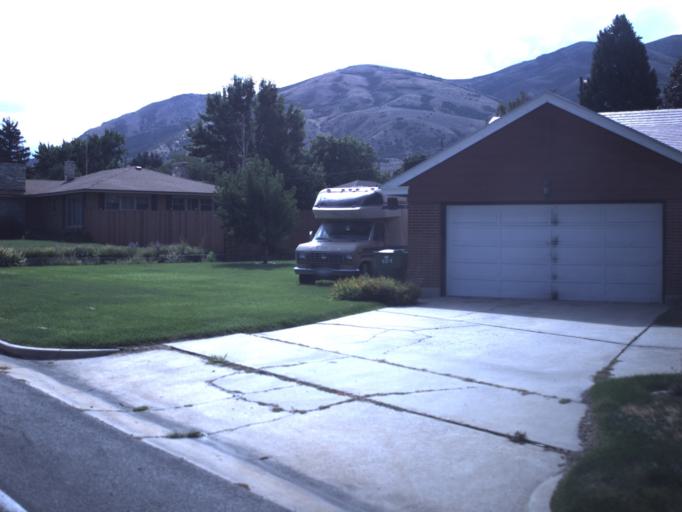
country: US
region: Utah
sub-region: Box Elder County
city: Brigham City
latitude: 41.5059
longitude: -112.0092
